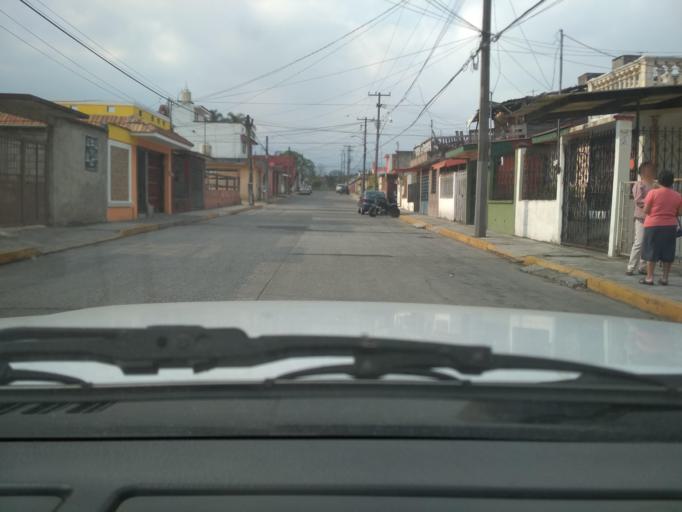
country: MX
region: Veracruz
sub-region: Mariano Escobedo
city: Palmira
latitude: 18.8732
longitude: -97.1006
